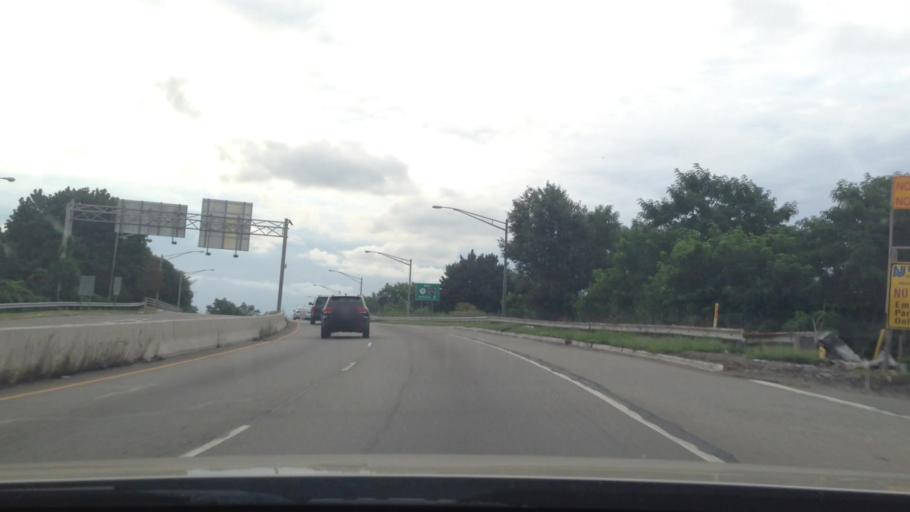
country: US
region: New Jersey
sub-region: Hudson County
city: Jersey City
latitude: 40.7461
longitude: -74.1017
